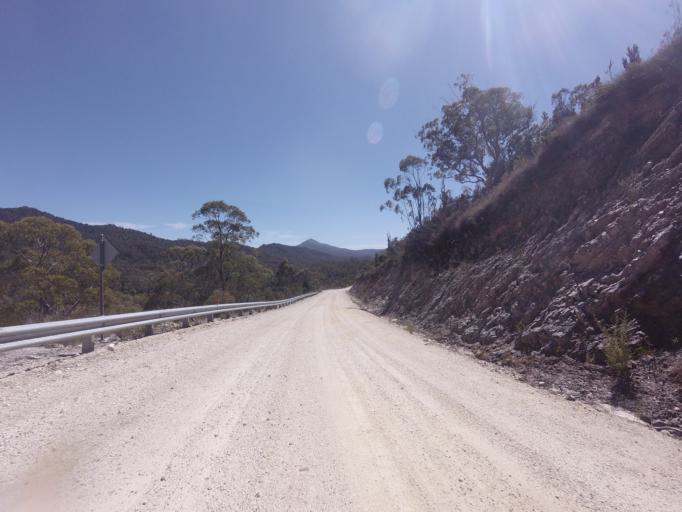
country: AU
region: Tasmania
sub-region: Huon Valley
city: Geeveston
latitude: -42.9317
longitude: 146.3419
